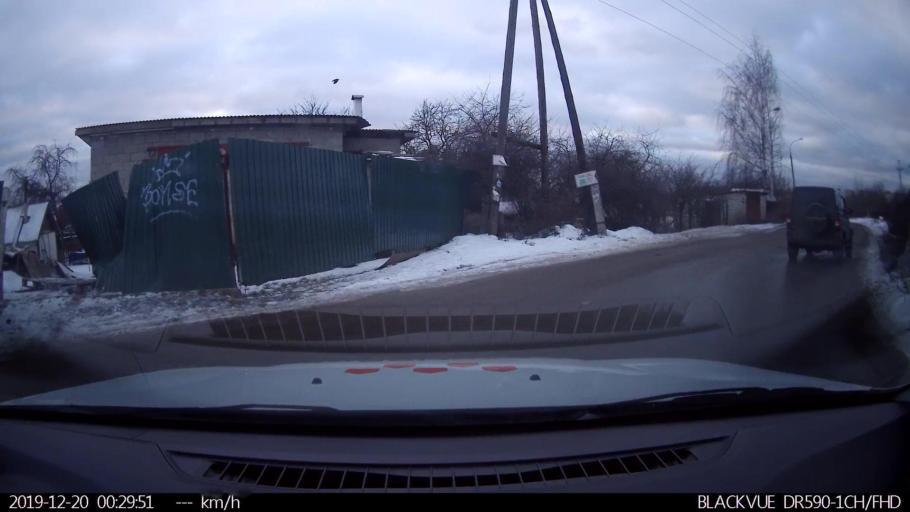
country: RU
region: Vladimir
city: Yur'yev-Pol'skiy
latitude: 56.5358
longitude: 39.6399
